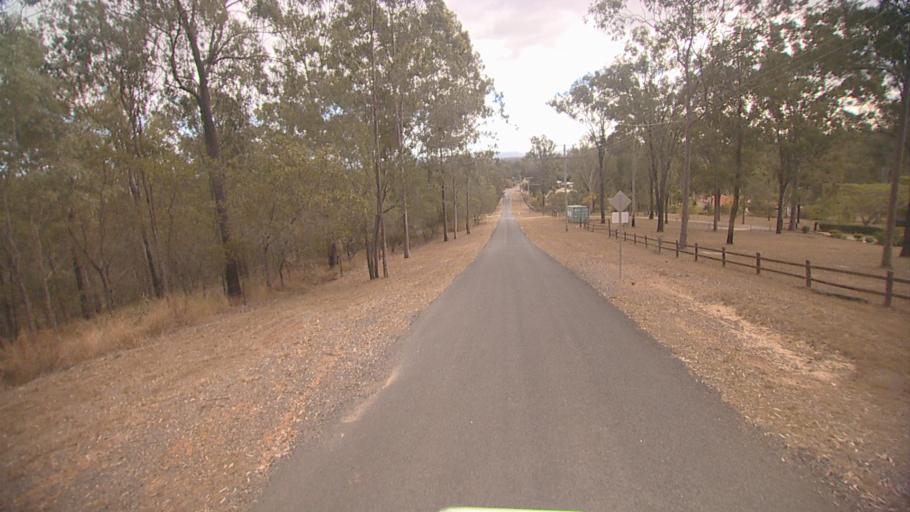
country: AU
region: Queensland
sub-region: Logan
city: Cedar Vale
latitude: -27.8577
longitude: 153.0640
